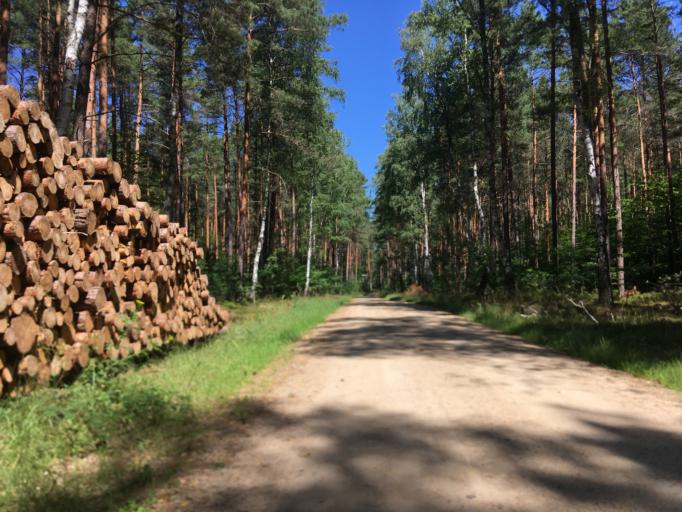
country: DE
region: Brandenburg
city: Rheinsberg
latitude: 53.1136
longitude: 12.9577
